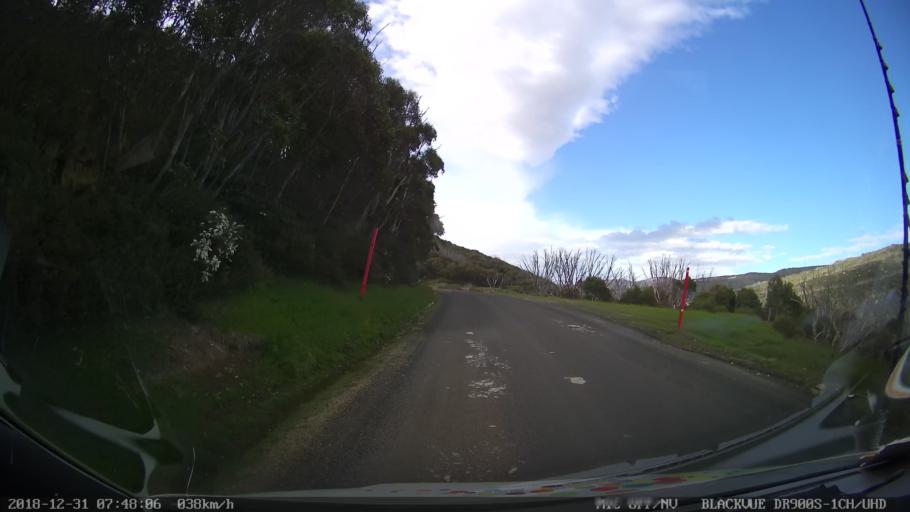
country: AU
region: New South Wales
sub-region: Snowy River
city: Jindabyne
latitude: -36.3669
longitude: 148.3930
